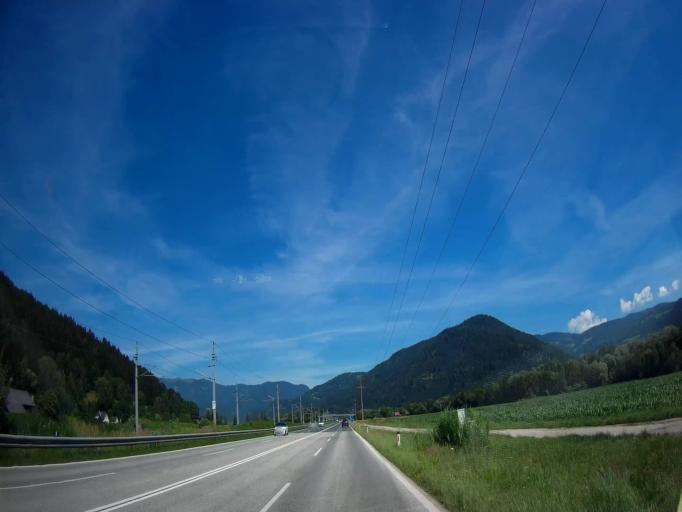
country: AT
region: Carinthia
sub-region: Politischer Bezirk Sankt Veit an der Glan
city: Micheldorf
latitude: 46.9343
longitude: 14.4262
